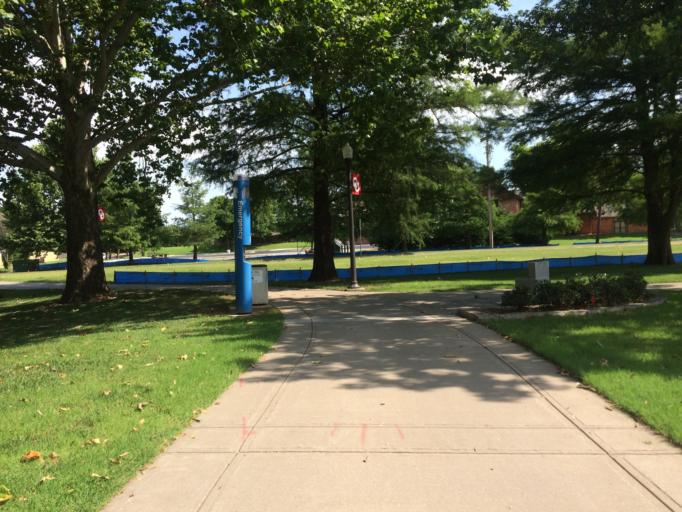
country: US
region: Oklahoma
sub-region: Cleveland County
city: Norman
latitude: 35.1962
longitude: -97.4497
